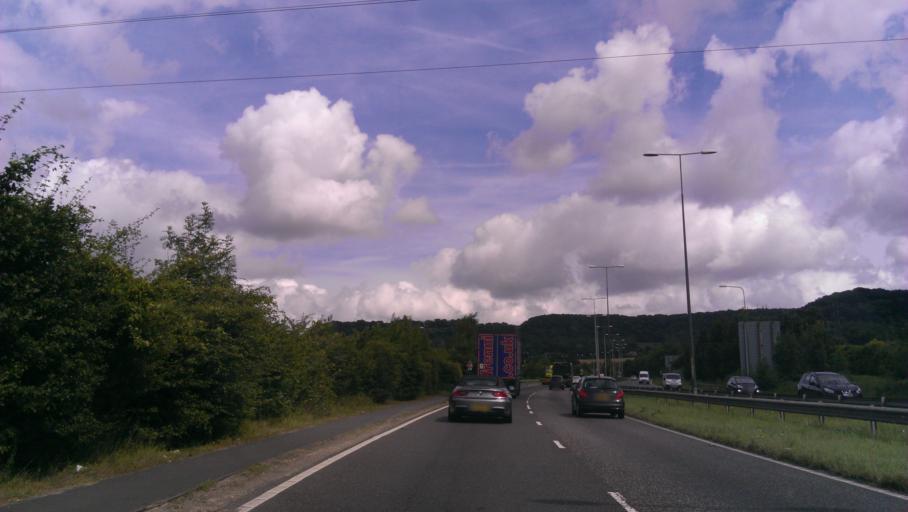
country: GB
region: England
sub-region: Kent
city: Boxley
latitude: 51.3065
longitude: 0.5119
